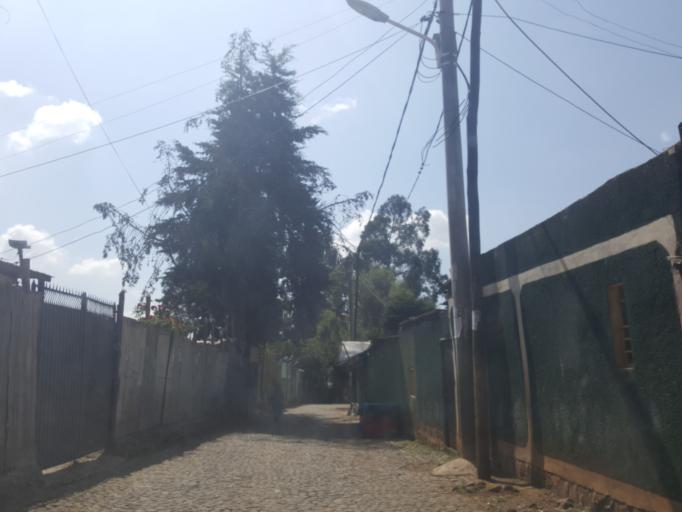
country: ET
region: Adis Abeba
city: Addis Ababa
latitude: 9.0556
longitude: 38.7294
